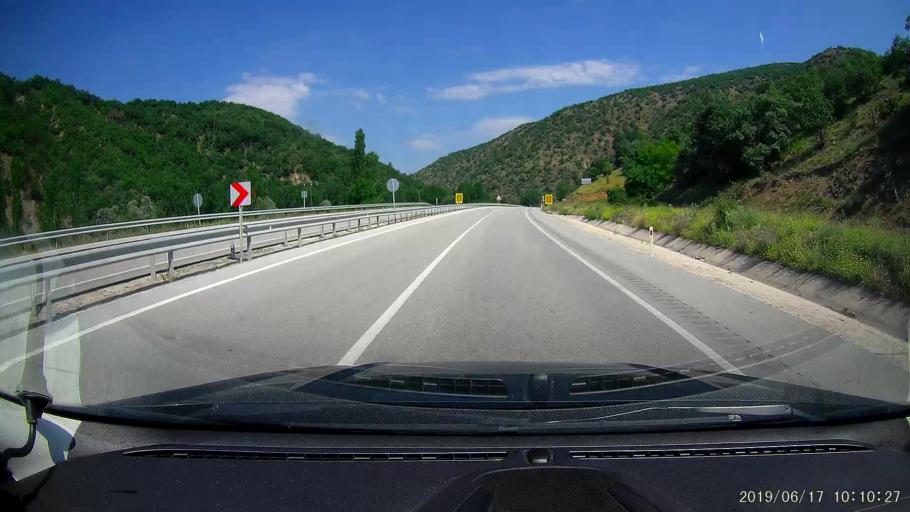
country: TR
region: Amasya
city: Saraycik
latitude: 40.9619
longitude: 35.0989
